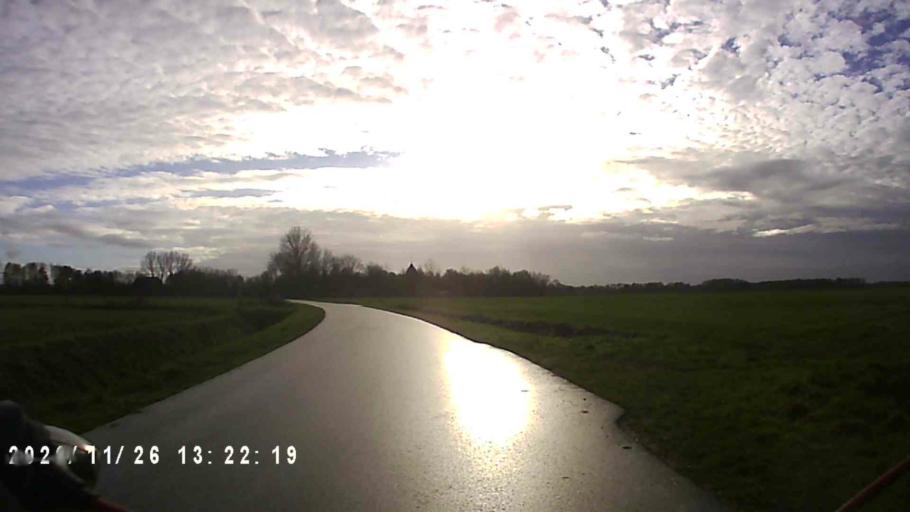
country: NL
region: Groningen
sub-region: Gemeente Delfzijl
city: Delfzijl
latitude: 53.3457
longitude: 6.8935
